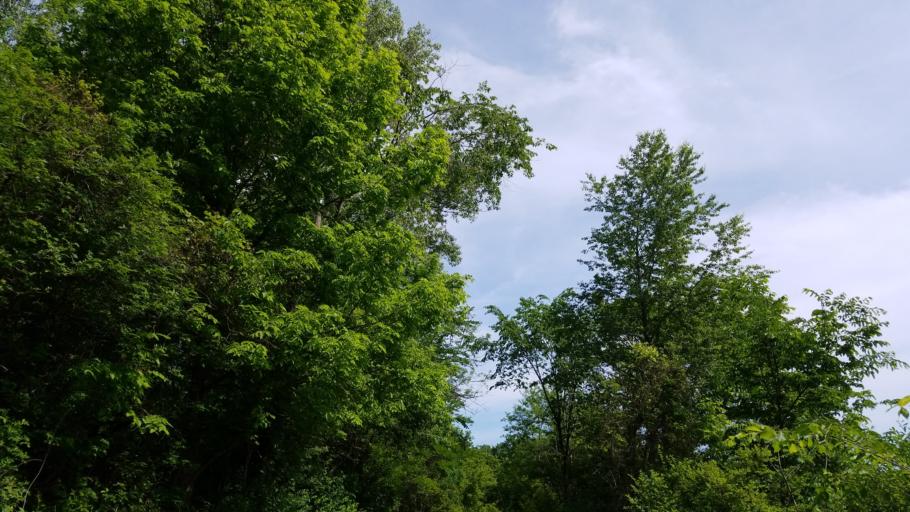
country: US
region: Wisconsin
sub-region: Dunn County
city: Menomonie
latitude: 44.7990
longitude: -91.9471
